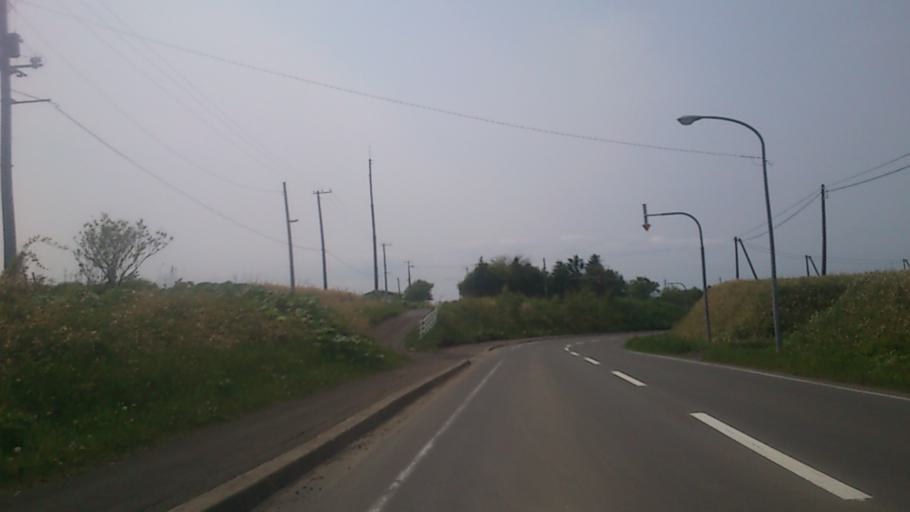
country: JP
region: Hokkaido
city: Nemuro
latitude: 43.2786
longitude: 145.5112
